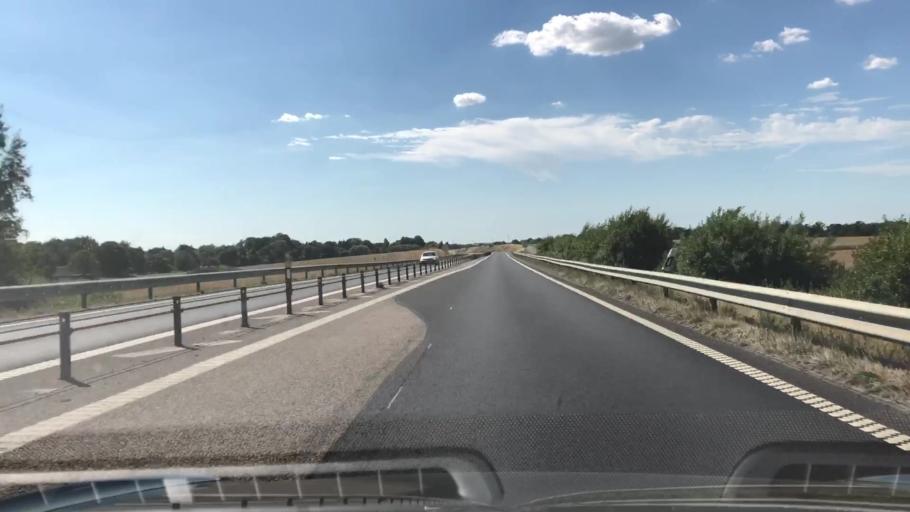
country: SE
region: Skane
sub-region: Horby Kommun
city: Hoerby
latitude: 55.8524
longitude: 13.6189
